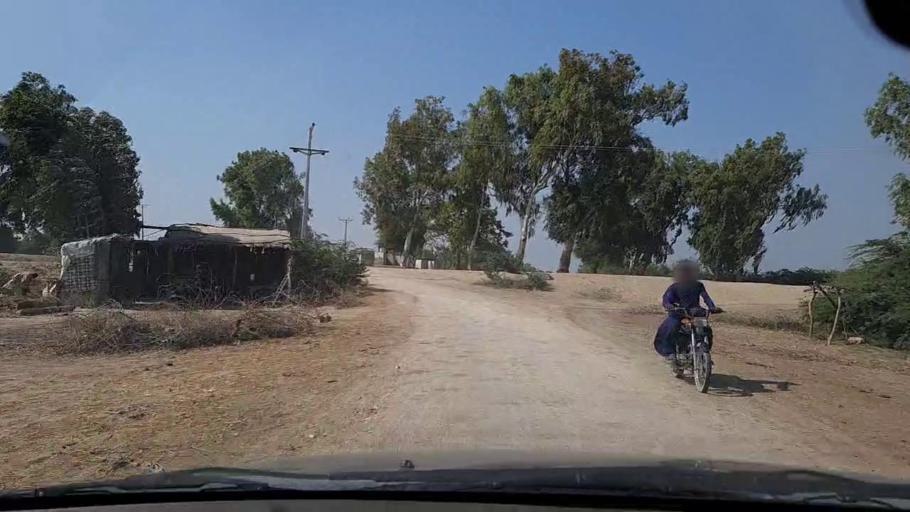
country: PK
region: Sindh
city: Chuhar Jamali
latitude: 24.4239
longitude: 67.8183
